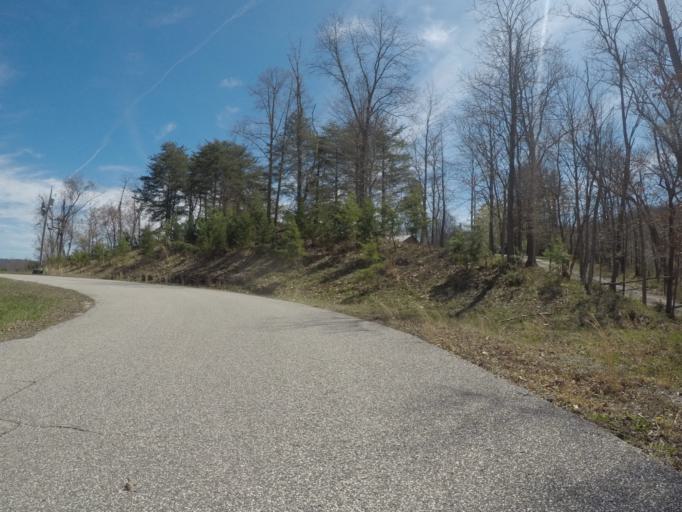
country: US
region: West Virginia
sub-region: Cabell County
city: Barboursville
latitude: 38.4074
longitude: -82.3057
